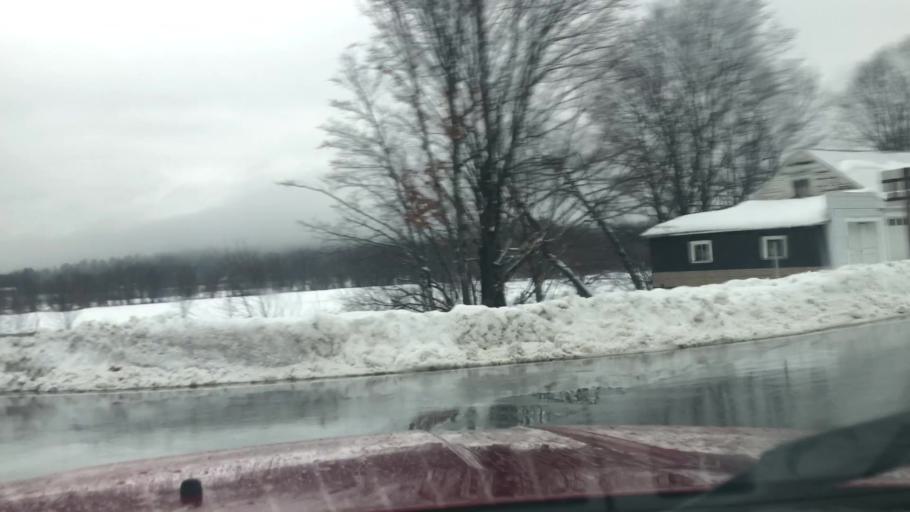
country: US
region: Maine
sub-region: Oxford County
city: Rumford
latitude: 44.5015
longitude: -70.6725
